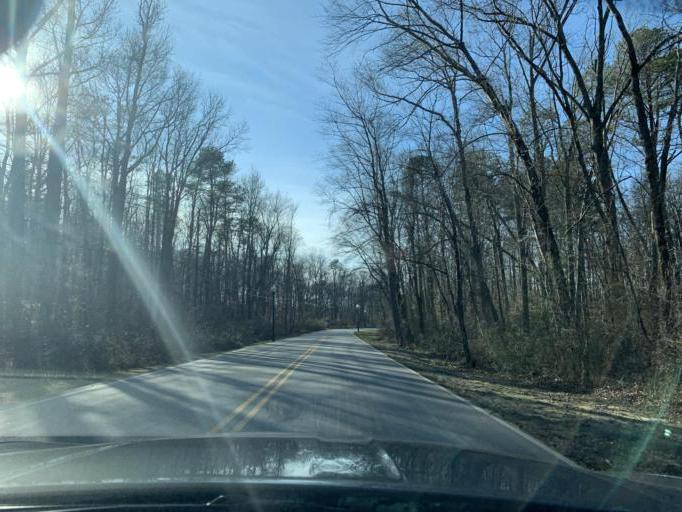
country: US
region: Maryland
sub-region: Anne Arundel County
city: Crofton
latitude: 39.0291
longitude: -76.7169
